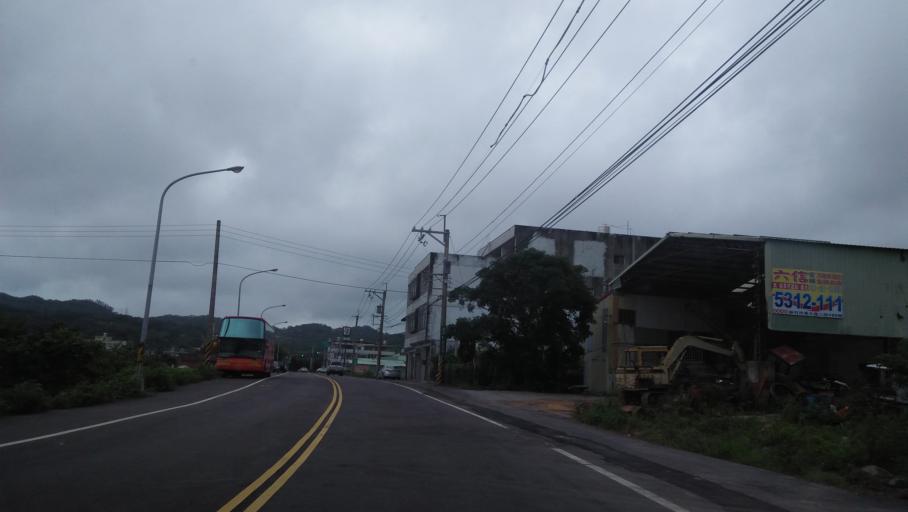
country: TW
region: Taiwan
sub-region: Hsinchu
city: Zhubei
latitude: 24.7882
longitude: 121.0657
